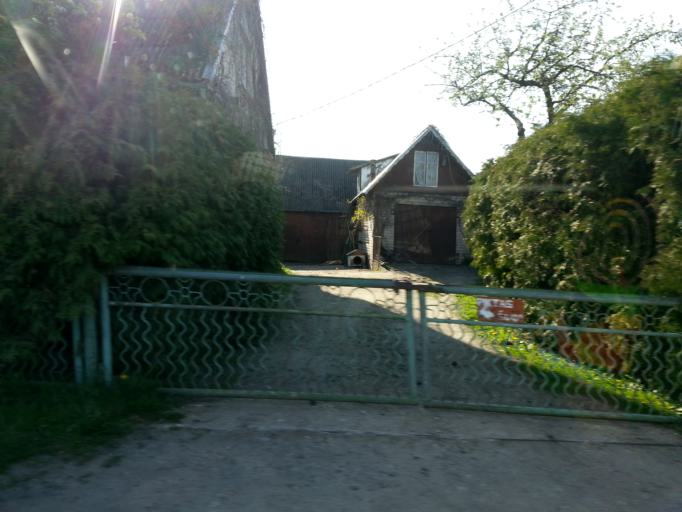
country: LT
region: Panevezys
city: Pasvalys
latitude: 55.9315
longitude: 24.3391
